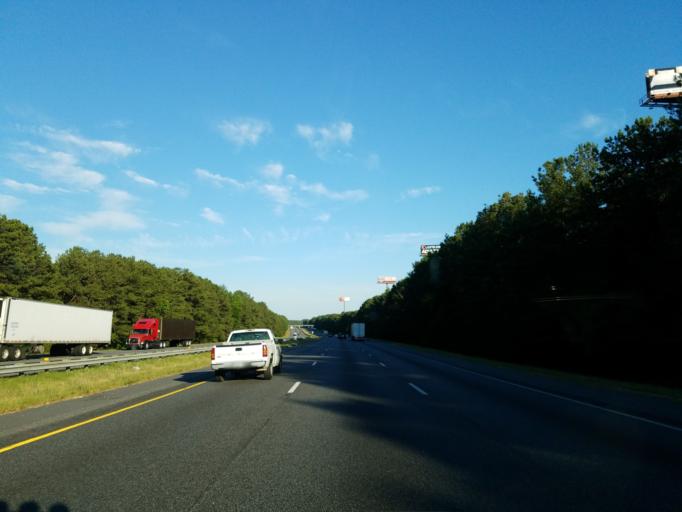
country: US
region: Georgia
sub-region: Bartow County
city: Adairsville
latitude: 34.3422
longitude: -84.8730
